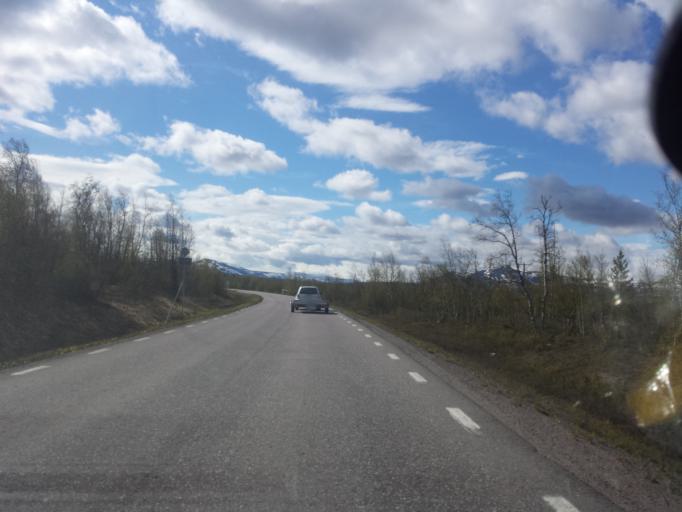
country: SE
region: Norrbotten
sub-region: Kiruna Kommun
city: Kiruna
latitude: 67.9947
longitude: 19.9015
